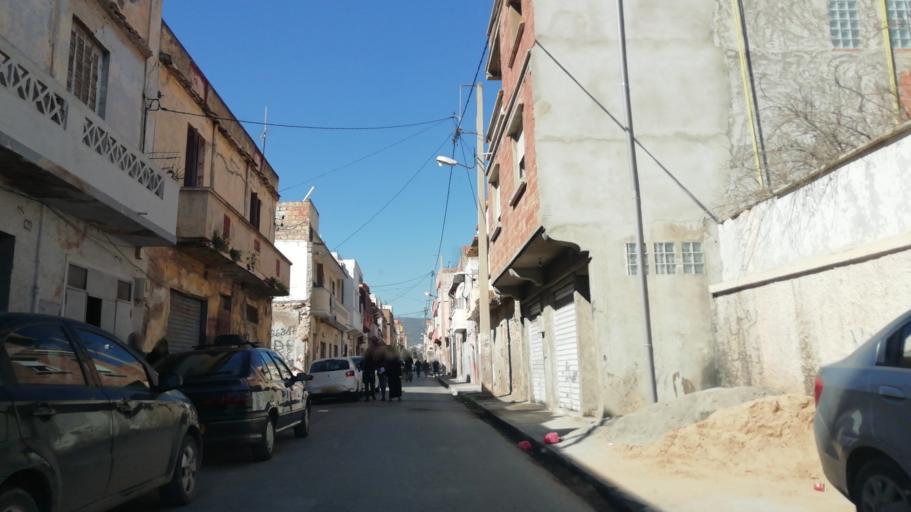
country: DZ
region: Oran
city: Oran
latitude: 35.6893
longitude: -0.6378
